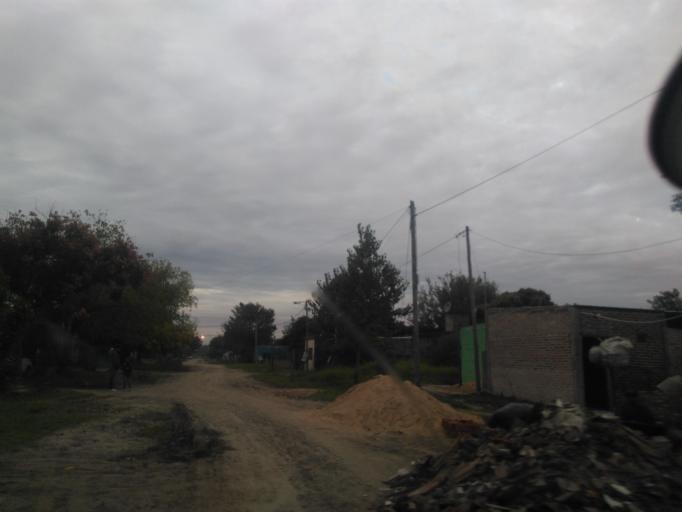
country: AR
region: Chaco
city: Resistencia
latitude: -27.4733
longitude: -59.0129
